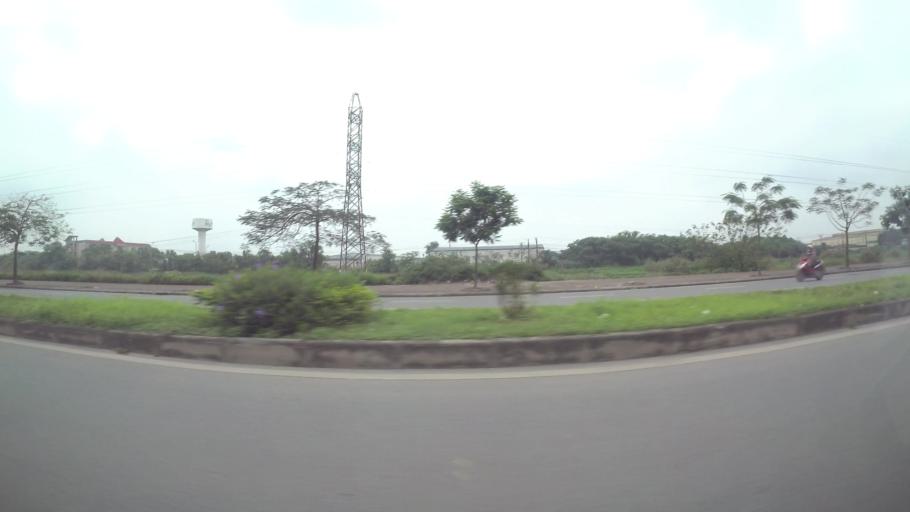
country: VN
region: Ha Noi
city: Trau Quy
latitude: 21.0343
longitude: 105.9255
